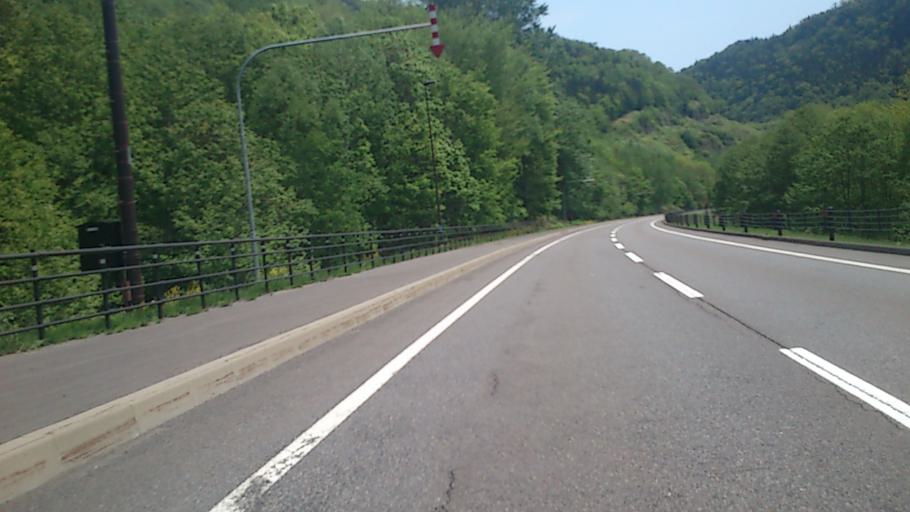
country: JP
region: Hokkaido
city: Otofuke
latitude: 43.3691
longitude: 143.2310
